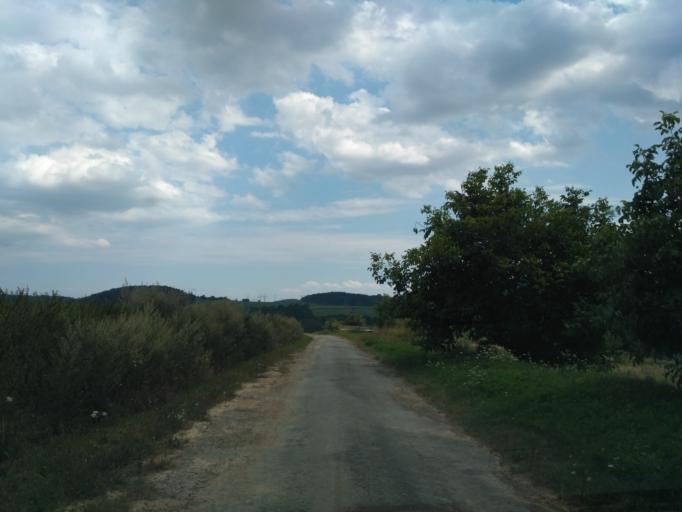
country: SK
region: Presovsky
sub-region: Okres Presov
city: Presov
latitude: 48.9127
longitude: 21.1782
